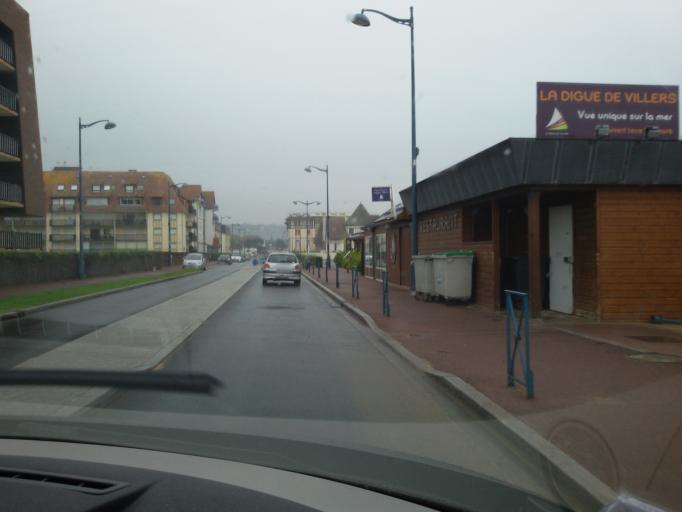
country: FR
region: Lower Normandy
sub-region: Departement du Calvados
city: Villers-sur-Mer
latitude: 49.3301
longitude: 0.0099
